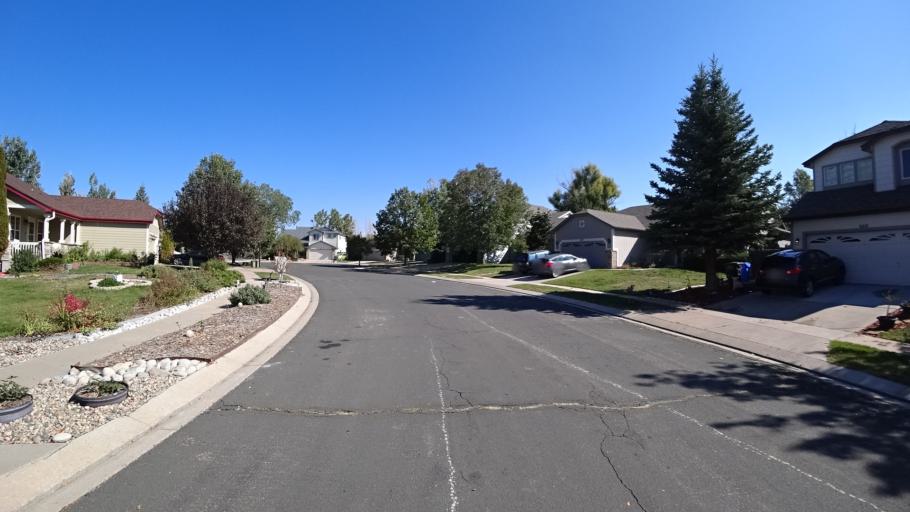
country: US
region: Colorado
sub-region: El Paso County
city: Cimarron Hills
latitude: 38.8789
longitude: -104.7062
